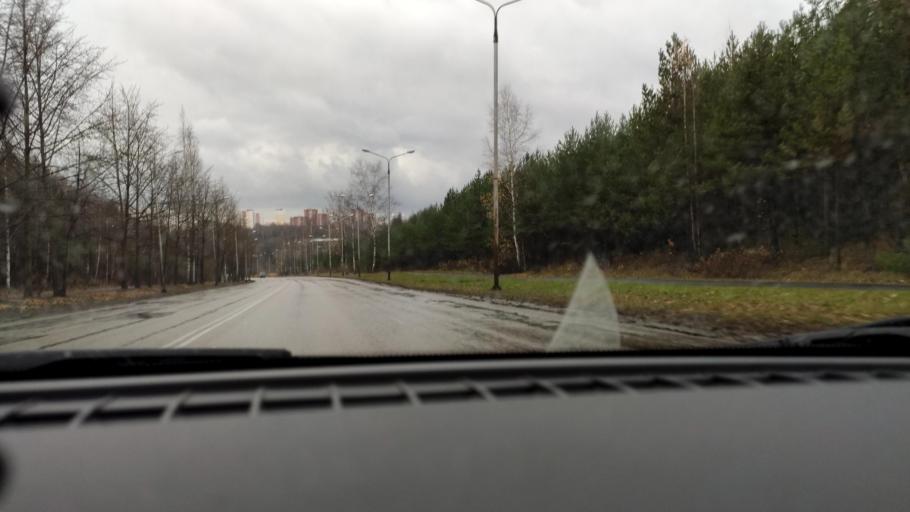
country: RU
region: Perm
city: Perm
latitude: 58.0760
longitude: 56.3698
